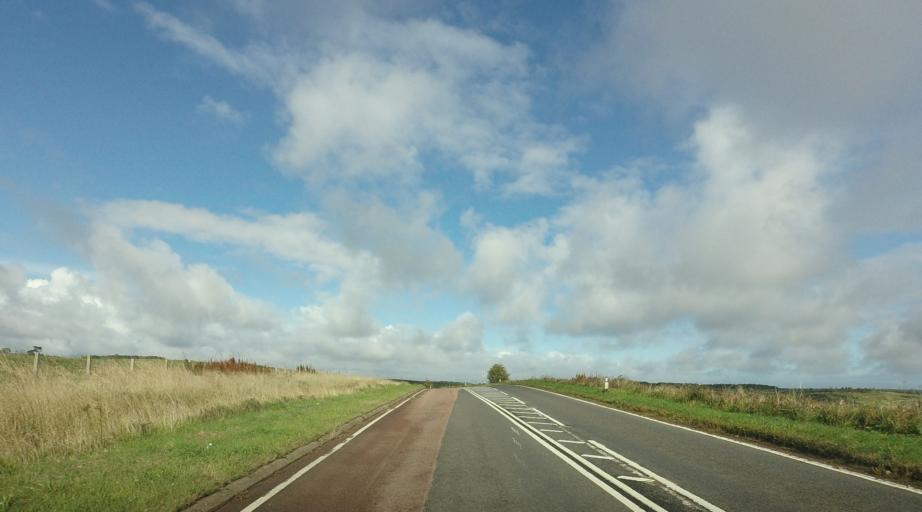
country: GB
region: Scotland
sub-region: Fife
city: Balmullo
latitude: 56.3801
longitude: -2.9233
